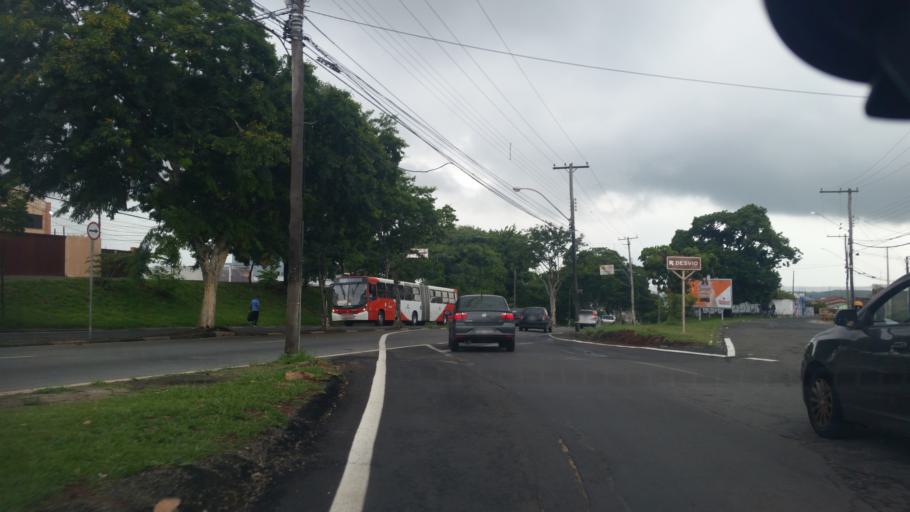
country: BR
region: Sao Paulo
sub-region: Campinas
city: Campinas
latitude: -22.9199
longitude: -47.1122
